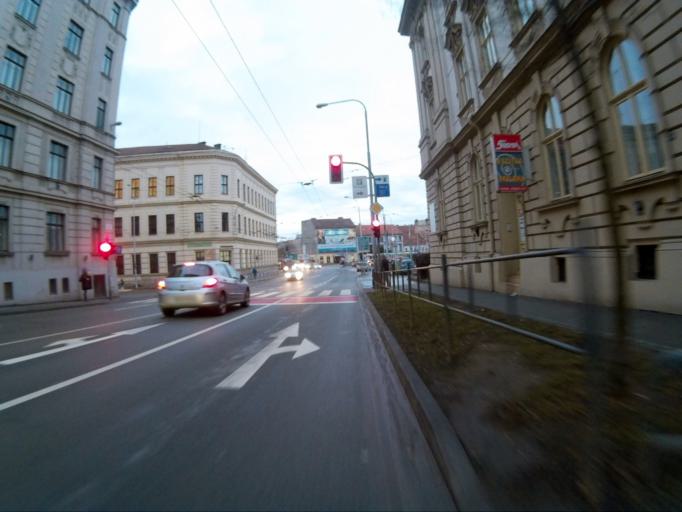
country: CZ
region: South Moravian
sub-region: Mesto Brno
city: Brno
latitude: 49.1921
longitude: 16.5957
